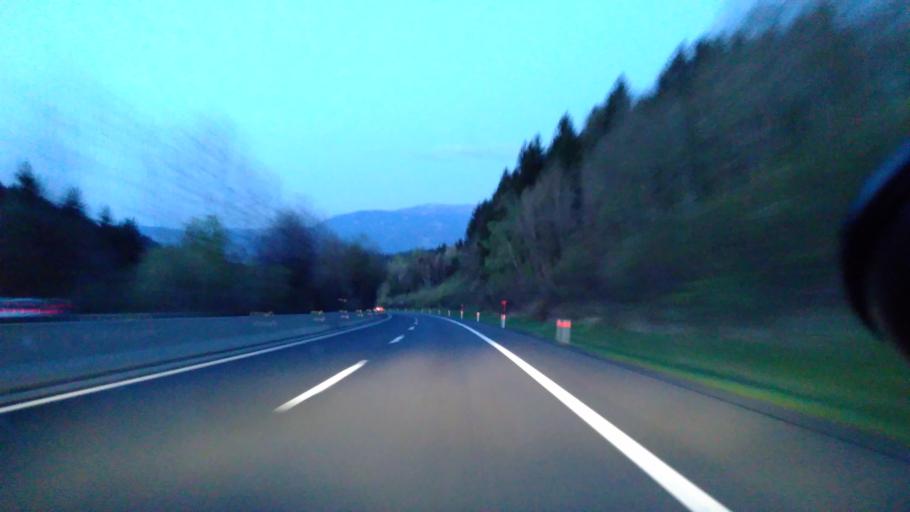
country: AT
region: Carinthia
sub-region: Politischer Bezirk Wolfsberg
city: Sankt Andrae
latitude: 46.7182
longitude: 14.7913
